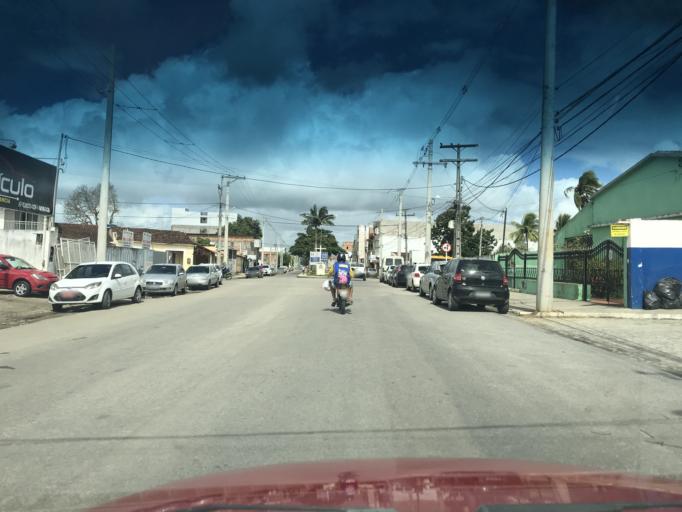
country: BR
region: Bahia
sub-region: Santo Antonio De Jesus
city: Santo Antonio de Jesus
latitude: -12.9681
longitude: -39.2706
